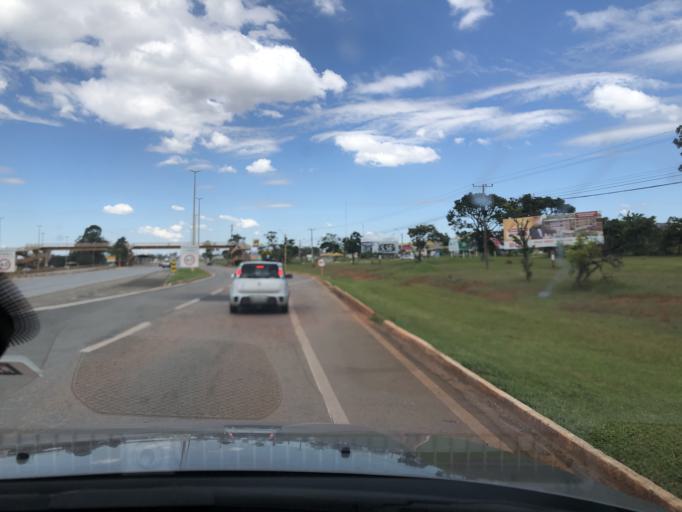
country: BR
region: Federal District
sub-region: Brasilia
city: Brasilia
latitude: -15.9901
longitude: -47.9871
